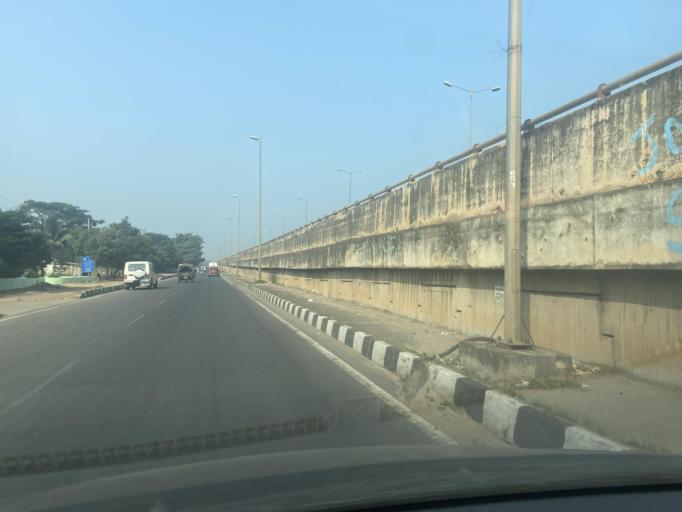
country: IN
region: Odisha
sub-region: Khordha
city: Bhubaneshwar
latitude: 20.2965
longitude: 85.8379
